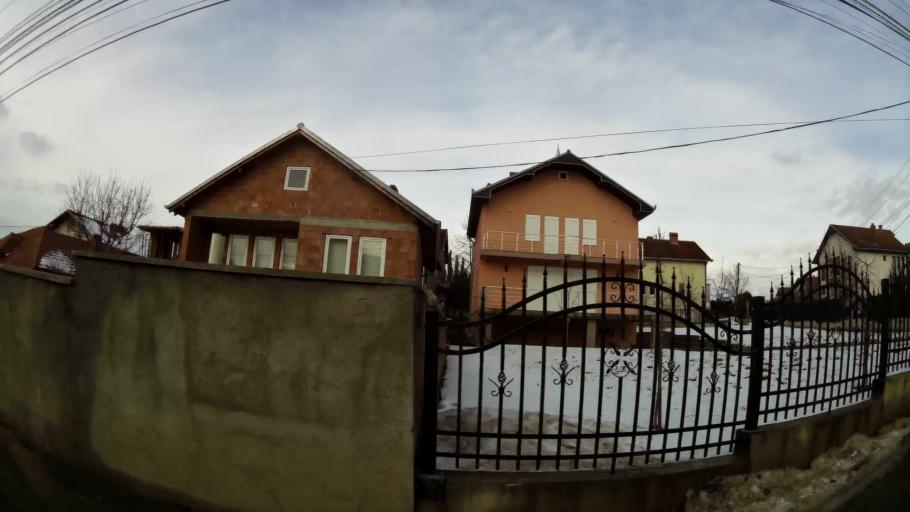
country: XK
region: Pristina
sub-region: Komuna e Prishtines
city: Pristina
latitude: 42.6719
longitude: 21.1875
